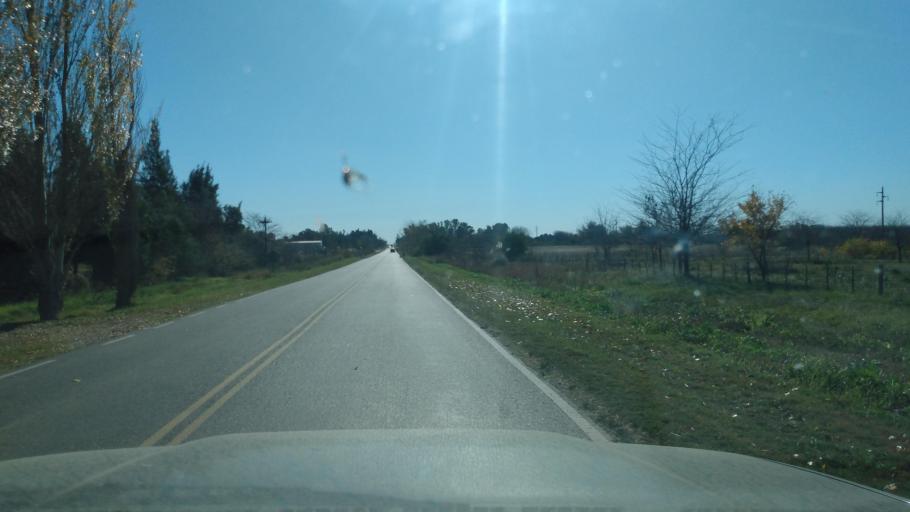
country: AR
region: Buenos Aires
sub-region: Partido de Lujan
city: Lujan
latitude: -34.5275
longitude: -59.1702
